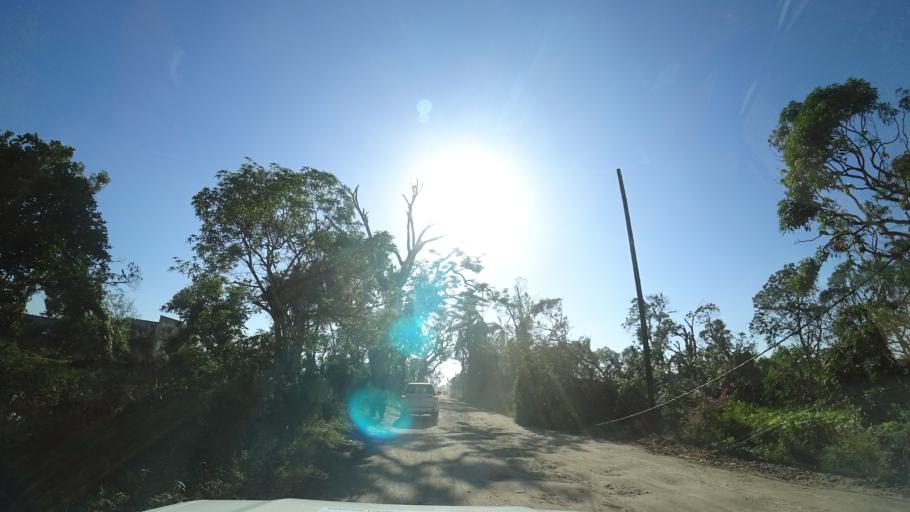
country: MZ
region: Sofala
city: Beira
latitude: -19.7657
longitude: 34.8956
